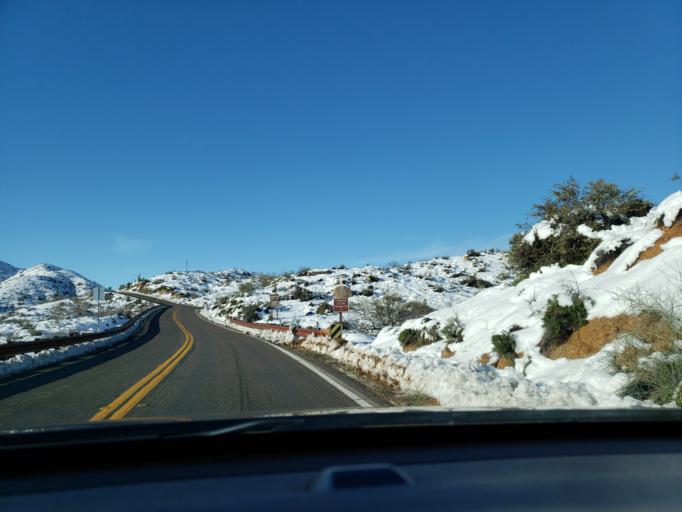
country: US
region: Arizona
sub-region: Maricopa County
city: Carefree
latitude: 33.8822
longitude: -111.8162
